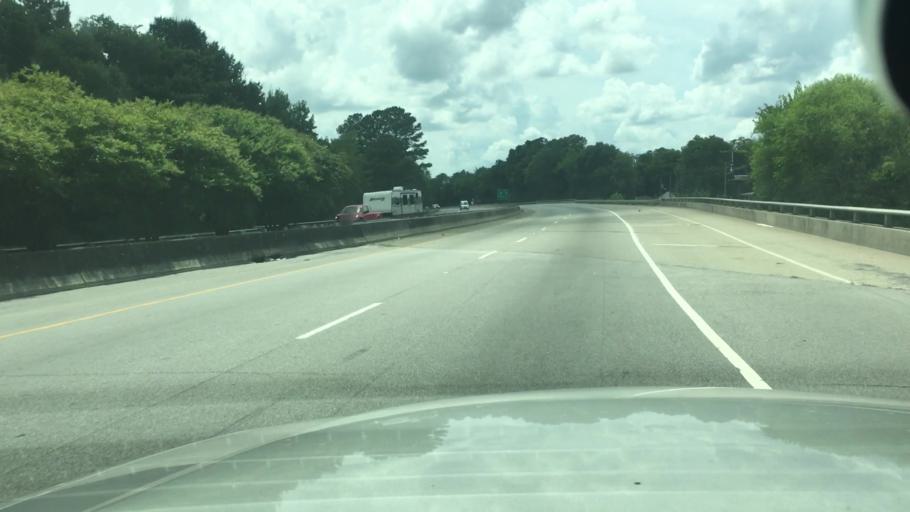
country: US
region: North Carolina
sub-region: Cumberland County
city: Fayetteville
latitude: 35.0701
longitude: -78.8818
